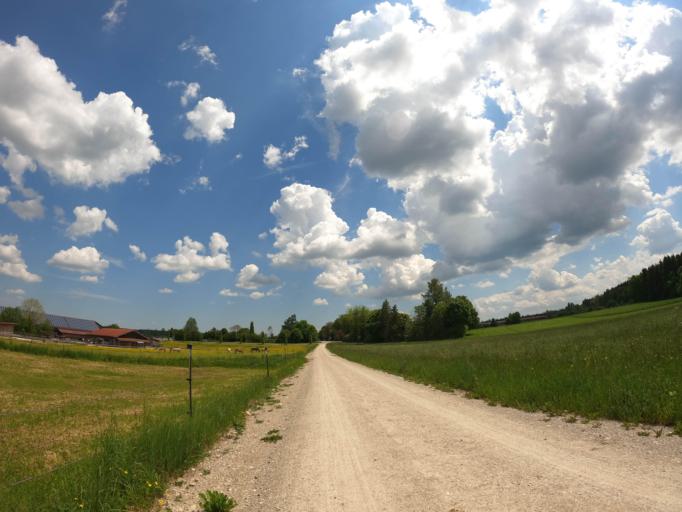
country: DE
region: Bavaria
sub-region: Upper Bavaria
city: Aying
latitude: 47.9583
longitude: 11.7566
